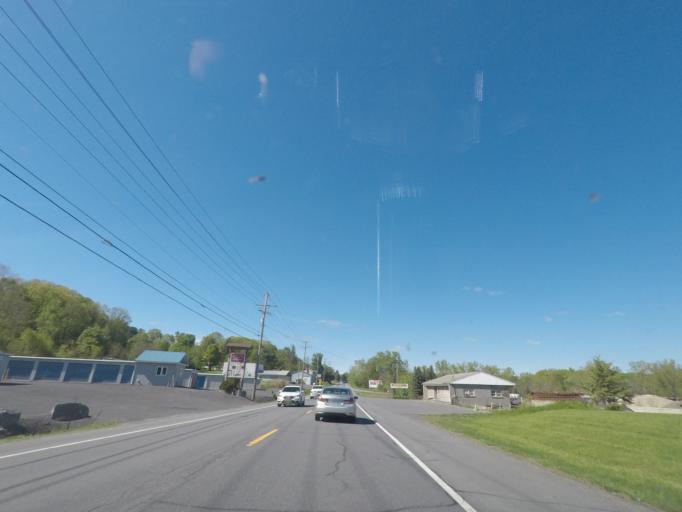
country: US
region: New York
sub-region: Albany County
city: Ravena
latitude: 42.4575
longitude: -73.8176
